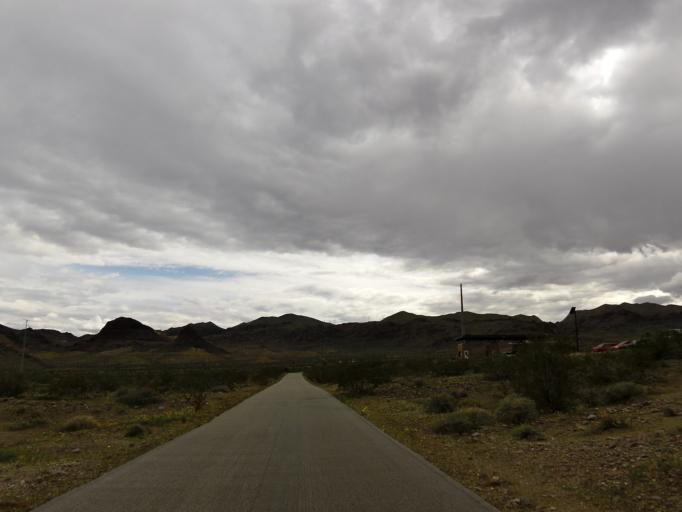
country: US
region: Nevada
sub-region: Clark County
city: Boulder City
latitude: 36.0218
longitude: -114.7961
